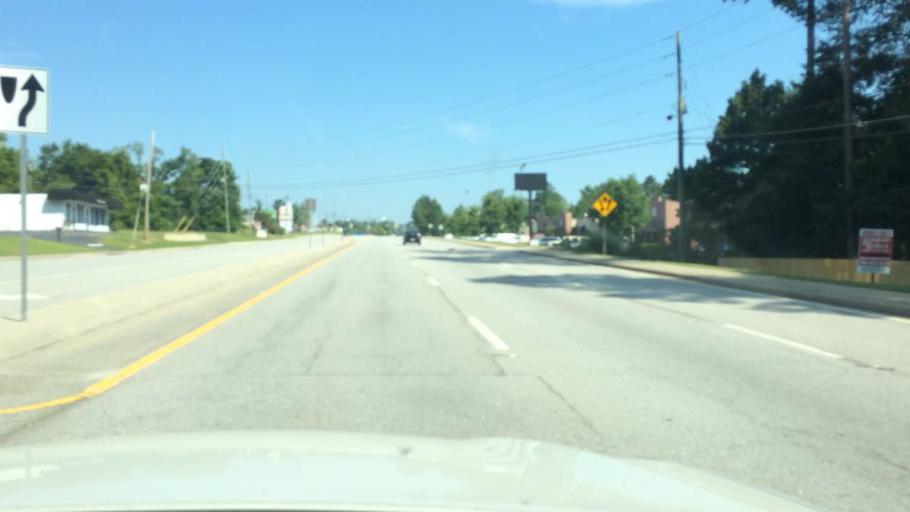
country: US
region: Georgia
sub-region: Columbia County
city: Martinez
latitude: 33.5252
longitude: -82.0699
